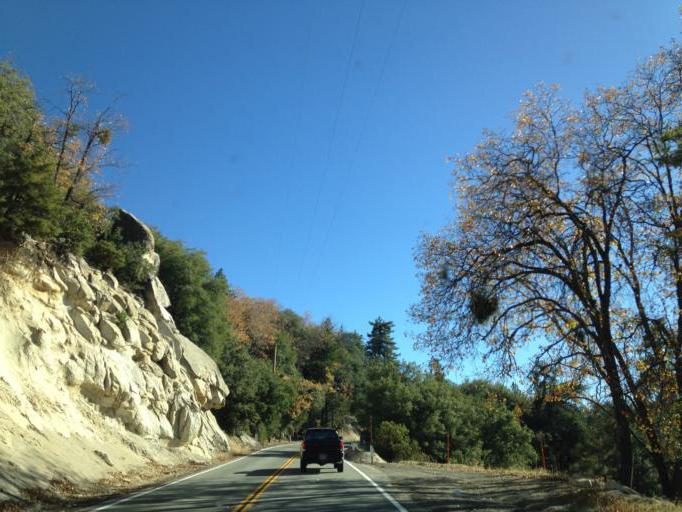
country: US
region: California
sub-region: Riverside County
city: Idyllwild-Pine Cove
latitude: 33.7683
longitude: -116.7408
